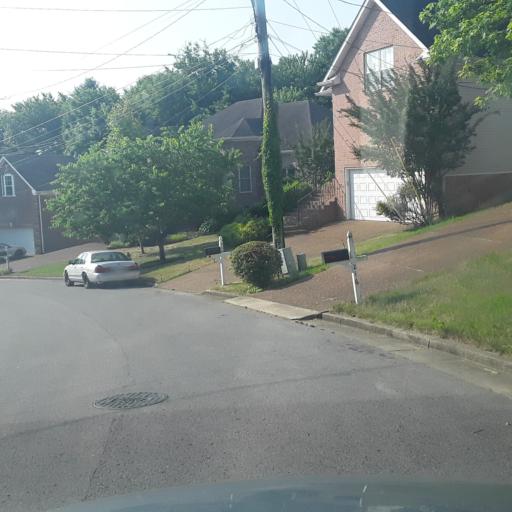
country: US
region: Tennessee
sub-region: Williamson County
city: Brentwood Estates
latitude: 36.0345
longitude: -86.7176
